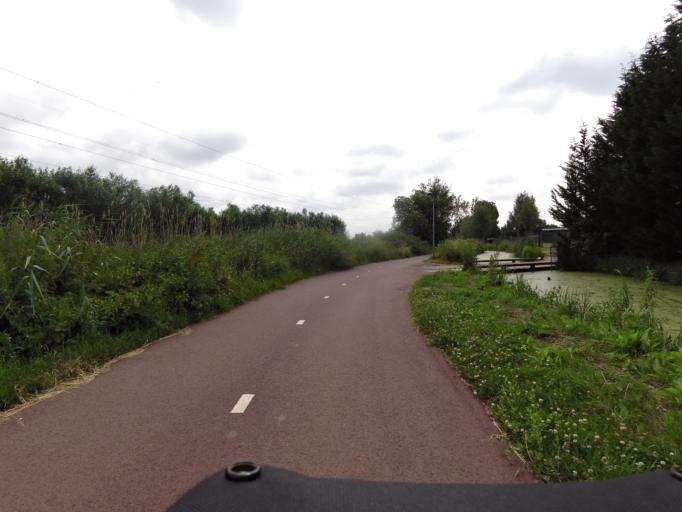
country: NL
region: South Holland
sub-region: Gemeente Schiedam
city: Schiedam
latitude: 51.9455
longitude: 4.3899
